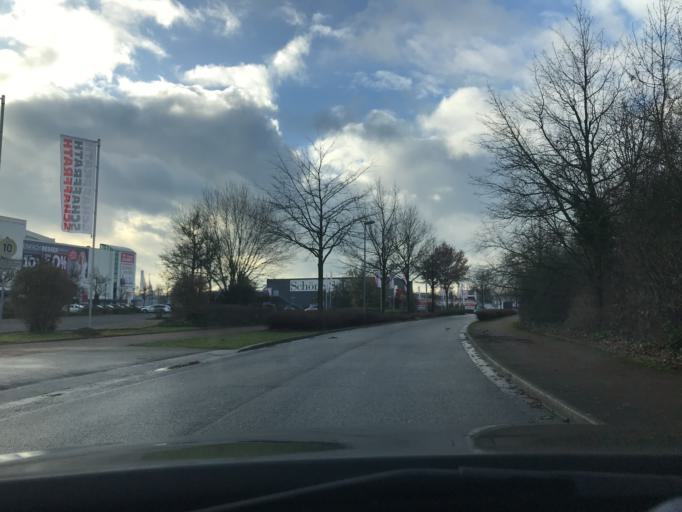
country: DE
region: North Rhine-Westphalia
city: Tonisvorst
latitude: 51.3496
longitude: 6.5347
